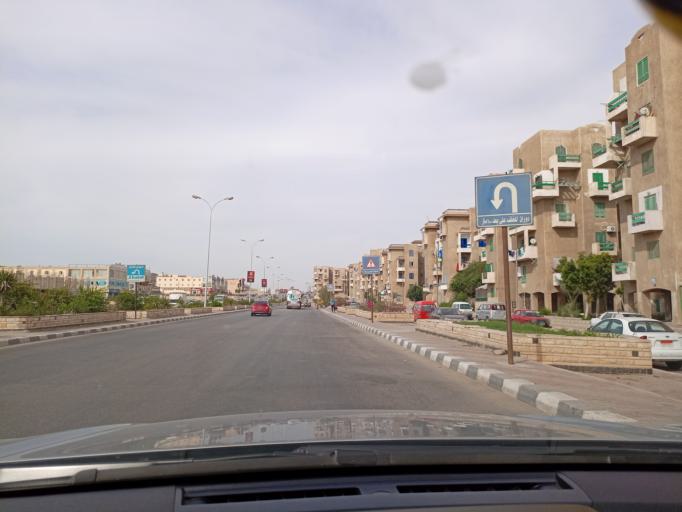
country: EG
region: Muhafazat al Qalyubiyah
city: Al Khankah
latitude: 30.2638
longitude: 31.4758
